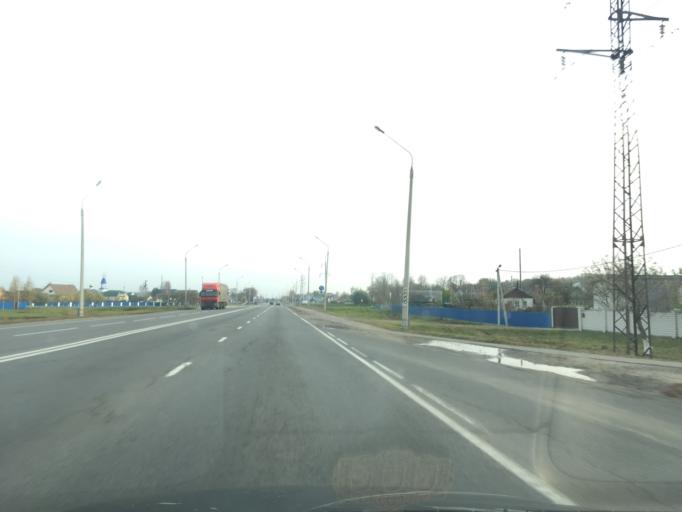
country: BY
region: Gomel
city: Kastsyukowka
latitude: 52.5128
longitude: 30.9401
